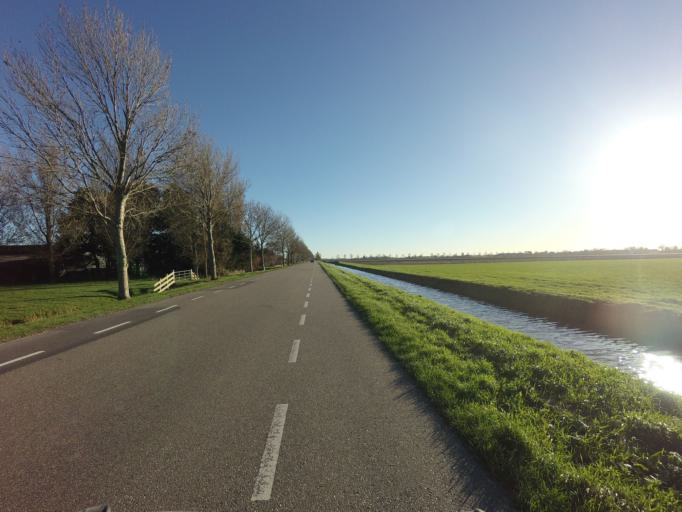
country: NL
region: South Holland
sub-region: Gemeente Nieuwkoop
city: Nieuwkoop
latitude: 52.1880
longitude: 4.7919
